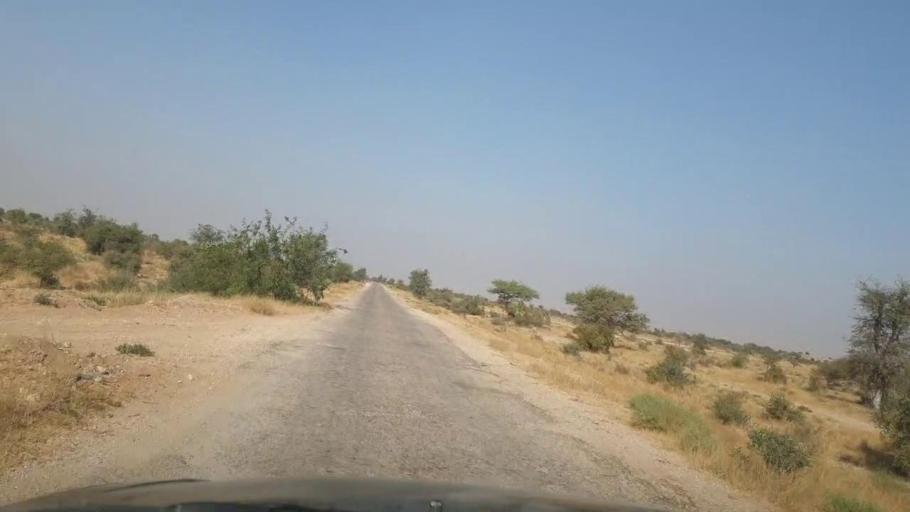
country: PK
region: Sindh
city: Jamshoro
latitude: 25.4802
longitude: 67.8229
